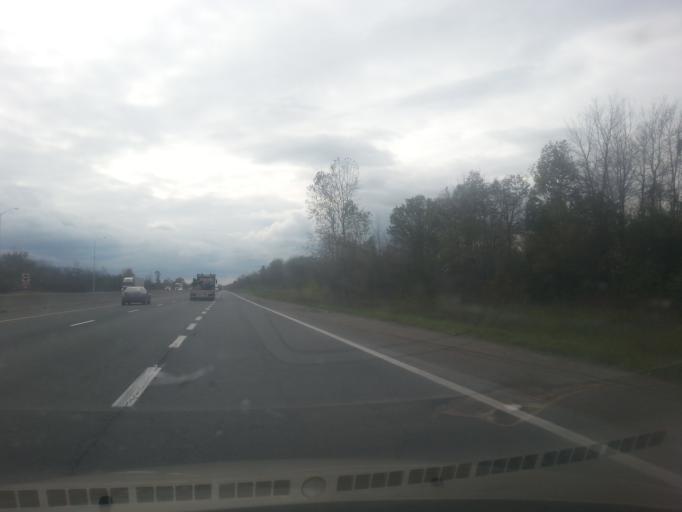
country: CA
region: Ontario
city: Belleville
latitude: 44.1791
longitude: -77.4517
